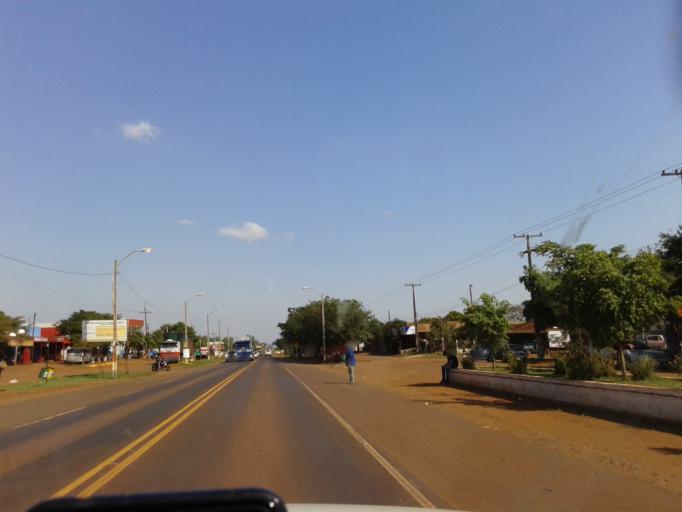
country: PY
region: Alto Parana
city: Santa Rita
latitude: -25.6636
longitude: -54.9937
